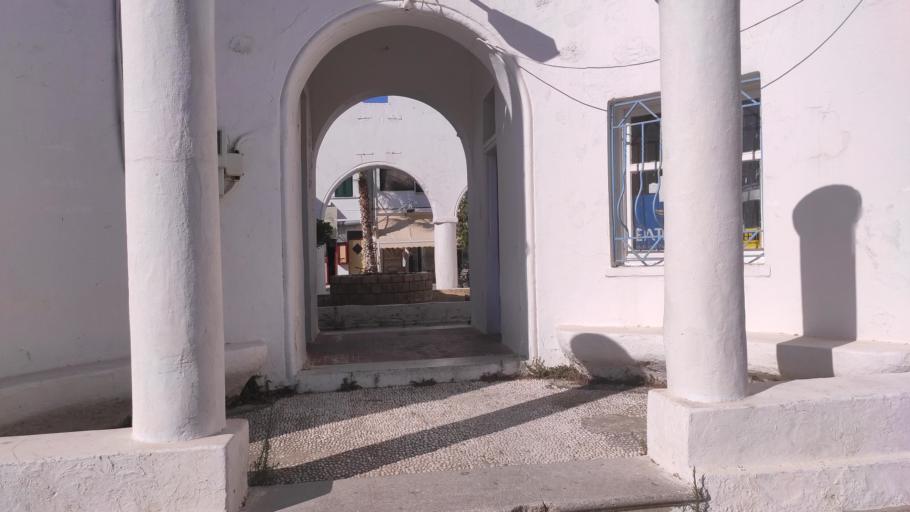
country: GR
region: South Aegean
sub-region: Nomos Dodekanisou
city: Kardamaina
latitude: 36.7821
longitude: 27.1439
